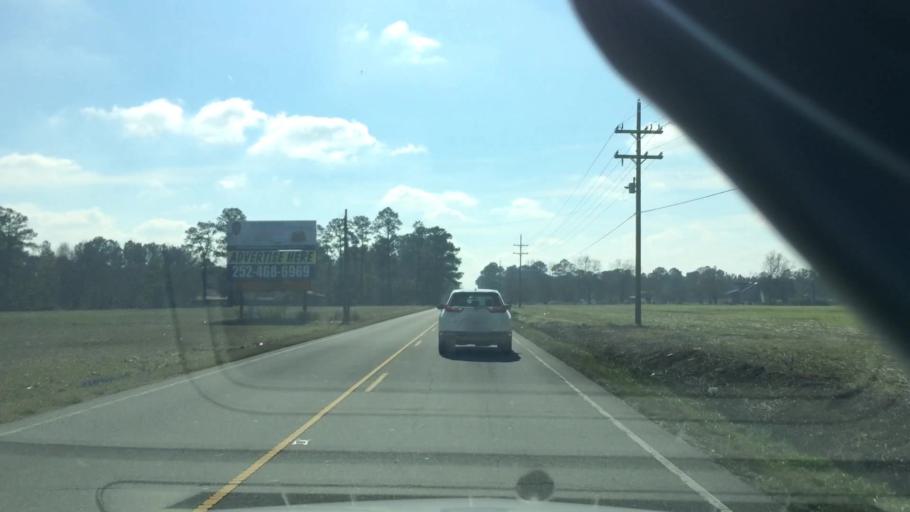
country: US
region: North Carolina
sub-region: Duplin County
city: Beulaville
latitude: 34.9032
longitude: -77.7795
